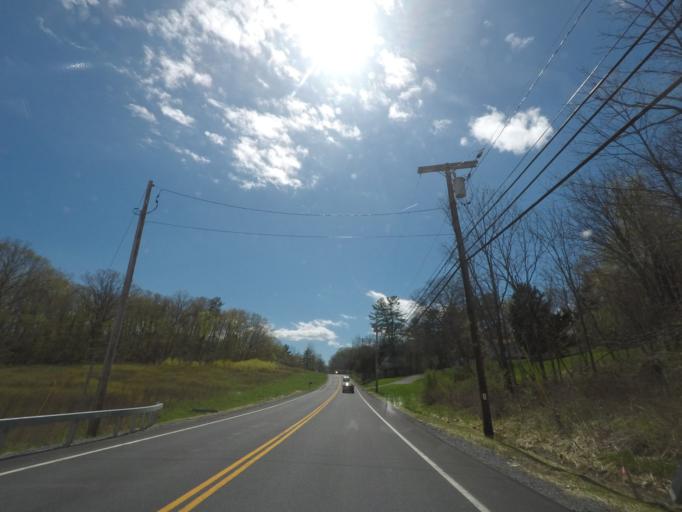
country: US
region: New York
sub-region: Greene County
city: Athens
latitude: 42.2508
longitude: -73.8383
